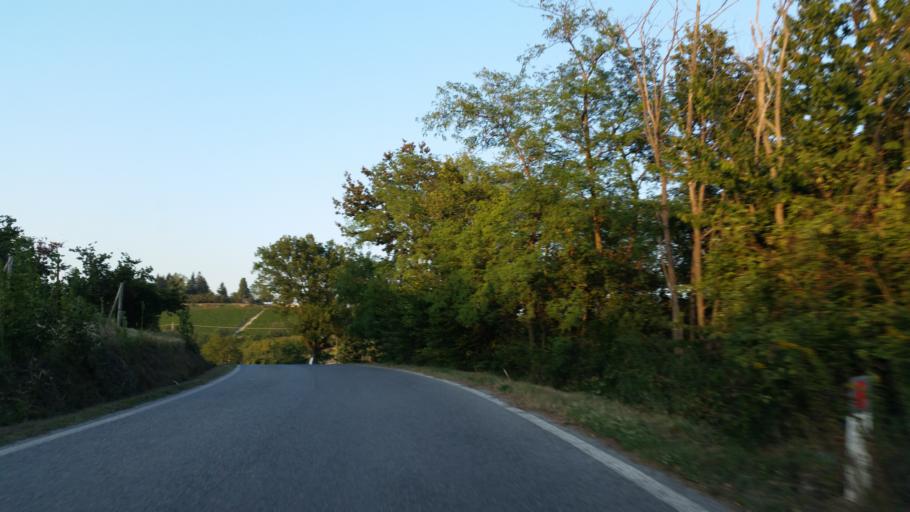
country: IT
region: Piedmont
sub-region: Provincia di Cuneo
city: Mango
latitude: 44.6663
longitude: 8.1359
